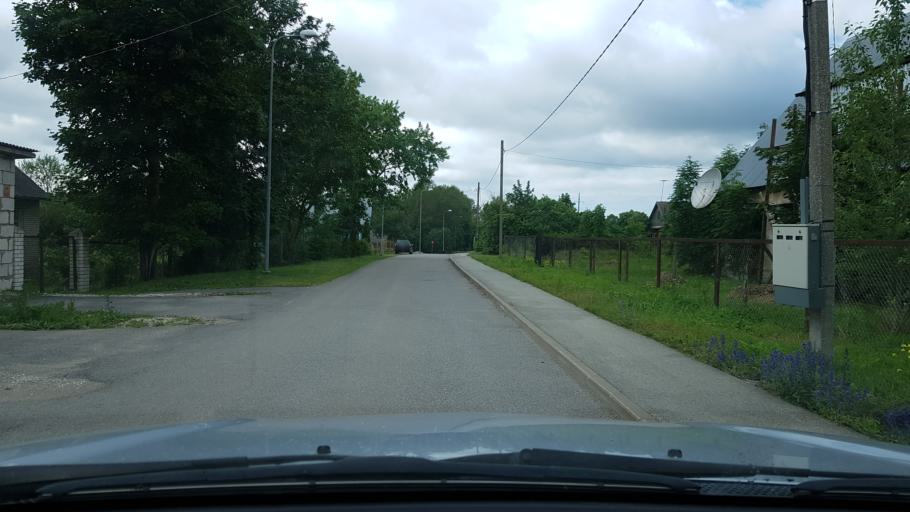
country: EE
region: Ida-Virumaa
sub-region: Narva linn
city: Narva
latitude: 59.3923
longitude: 28.1281
